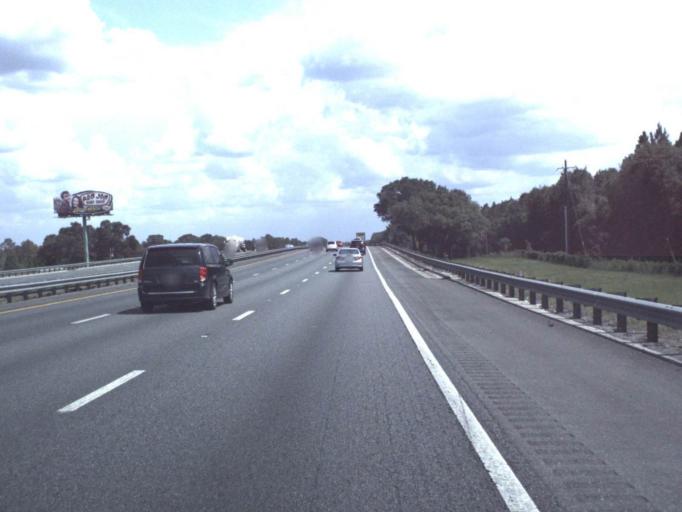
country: US
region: Florida
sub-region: Columbia County
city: Lake City
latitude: 30.1490
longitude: -82.6731
